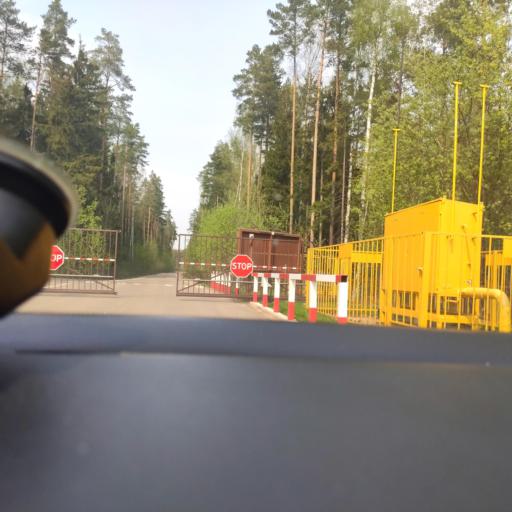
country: RU
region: Moskovskaya
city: Nakhabino
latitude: 55.8094
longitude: 37.1740
